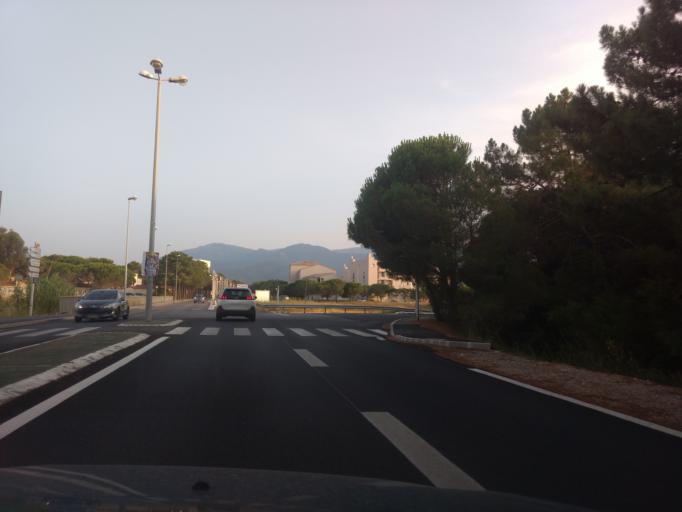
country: FR
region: Languedoc-Roussillon
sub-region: Departement des Pyrenees-Orientales
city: Argelers
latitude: 42.5670
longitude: 3.0412
